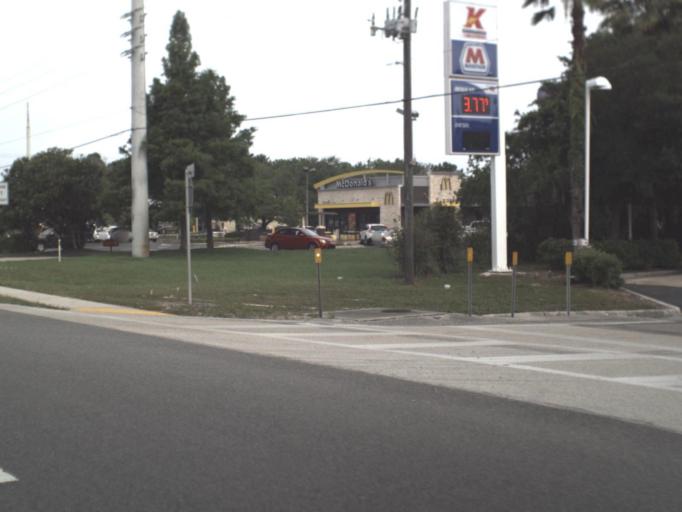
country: US
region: Florida
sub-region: Saint Johns County
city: Saint Augustine
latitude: 29.9167
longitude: -81.4083
